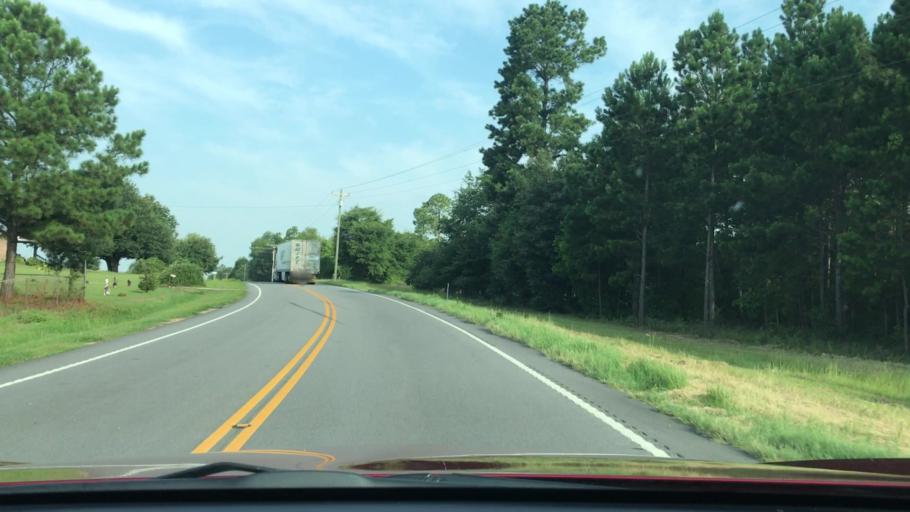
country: US
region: South Carolina
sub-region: Barnwell County
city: Blackville
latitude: 33.5604
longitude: -81.1695
